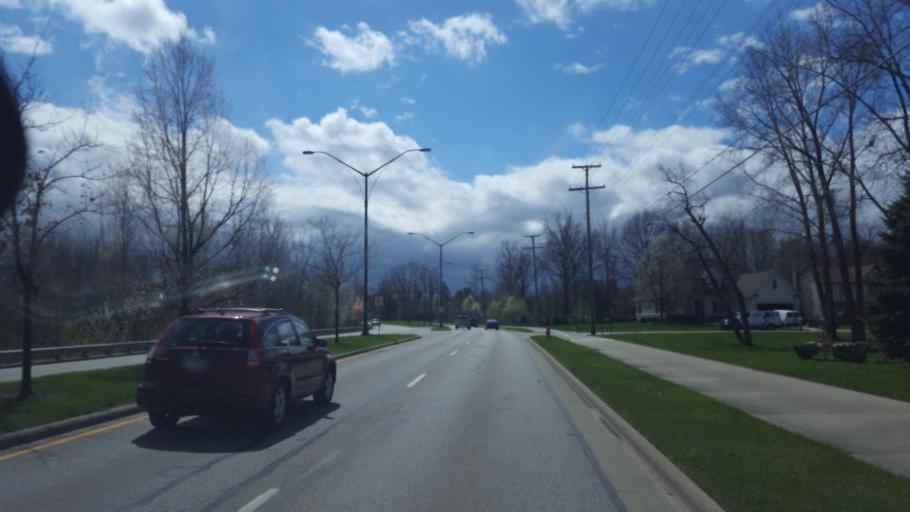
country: US
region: Ohio
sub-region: Franklin County
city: Westerville
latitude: 40.1263
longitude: -82.8875
